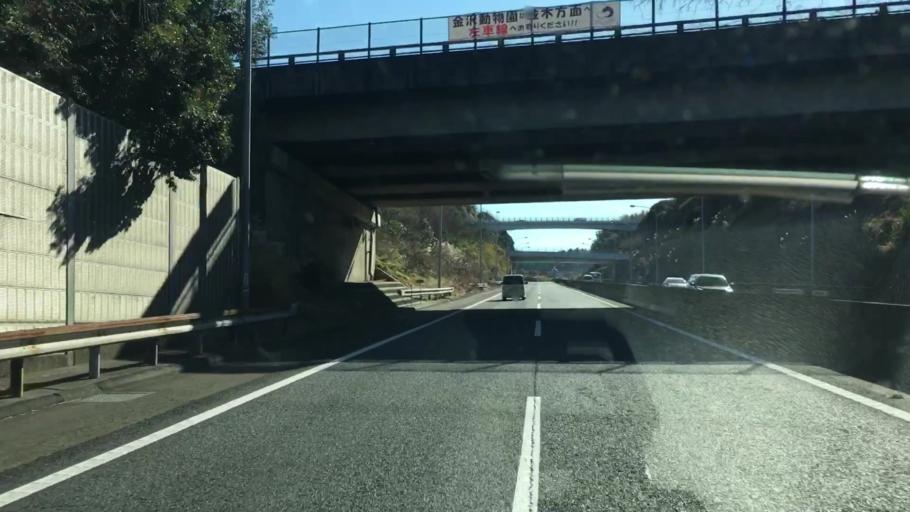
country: JP
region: Kanagawa
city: Kamakura
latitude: 35.3701
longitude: 139.5943
